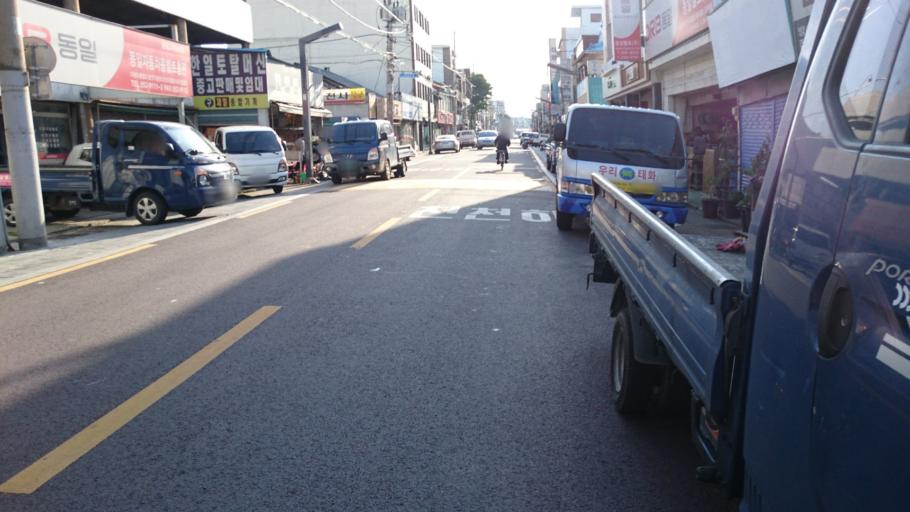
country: KR
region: Daegu
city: Daegu
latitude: 35.8743
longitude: 128.5930
